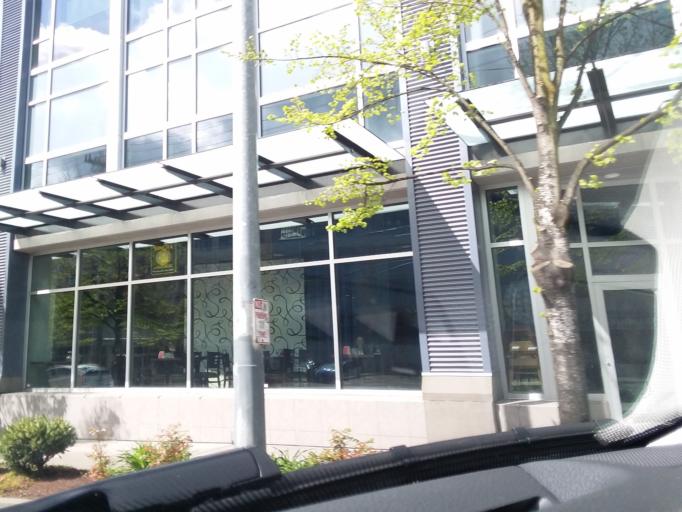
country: US
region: Washington
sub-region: King County
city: Seattle
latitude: 47.6345
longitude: -122.3254
